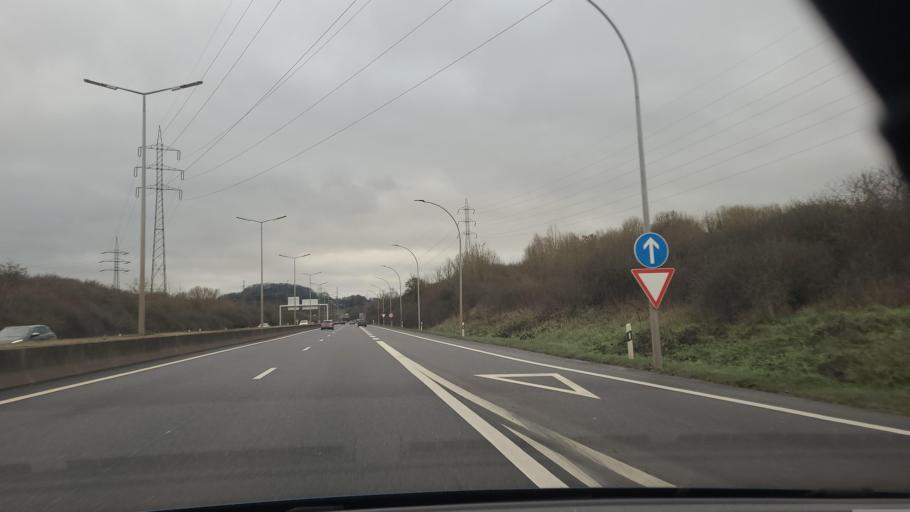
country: LU
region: Luxembourg
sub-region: Canton d'Esch-sur-Alzette
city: Sanem
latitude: 49.5427
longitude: 5.9193
